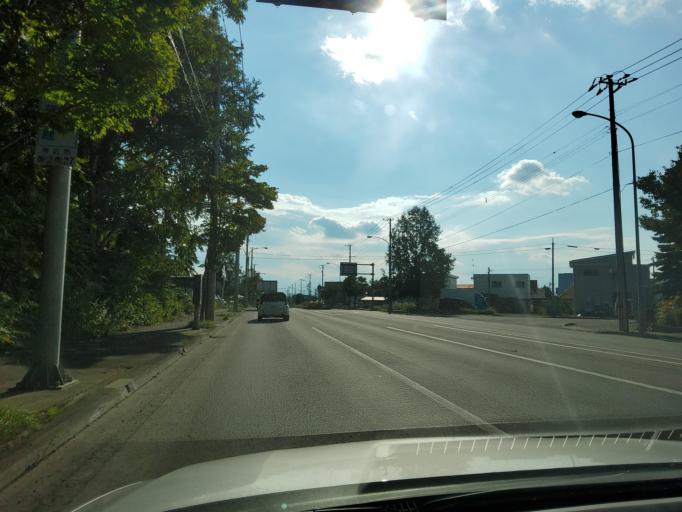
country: JP
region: Hokkaido
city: Obihiro
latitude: 42.9014
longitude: 143.2119
